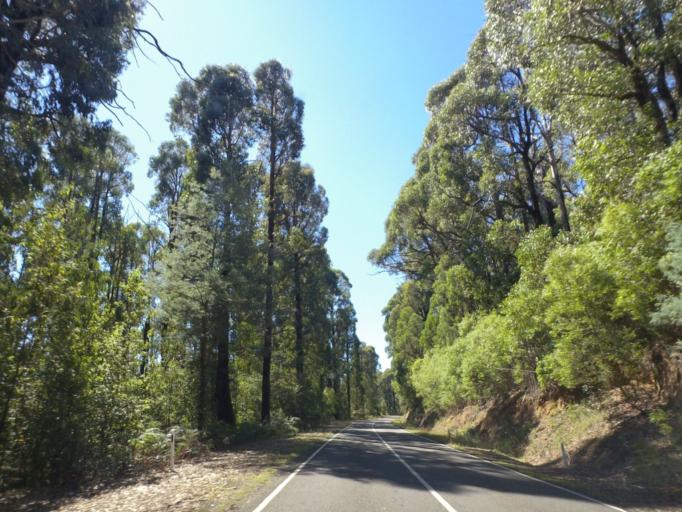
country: AU
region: Victoria
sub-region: Yarra Ranges
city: Millgrove
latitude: -37.5207
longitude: 145.7934
